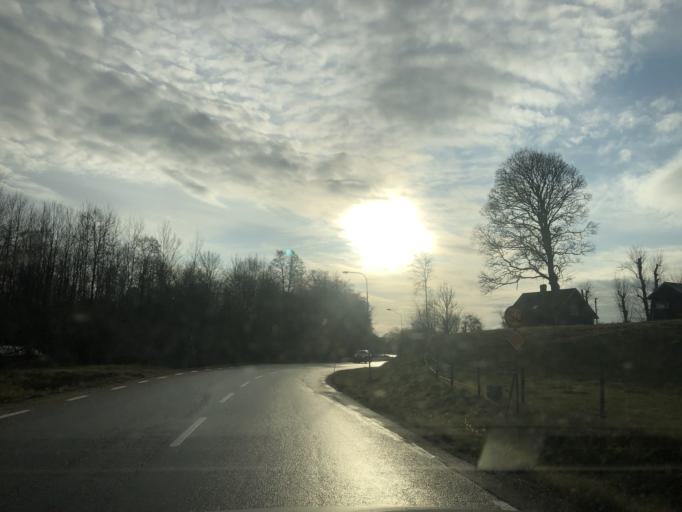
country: SE
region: Vaestra Goetaland
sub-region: Ulricehamns Kommun
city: Ulricehamn
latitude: 57.7451
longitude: 13.4186
